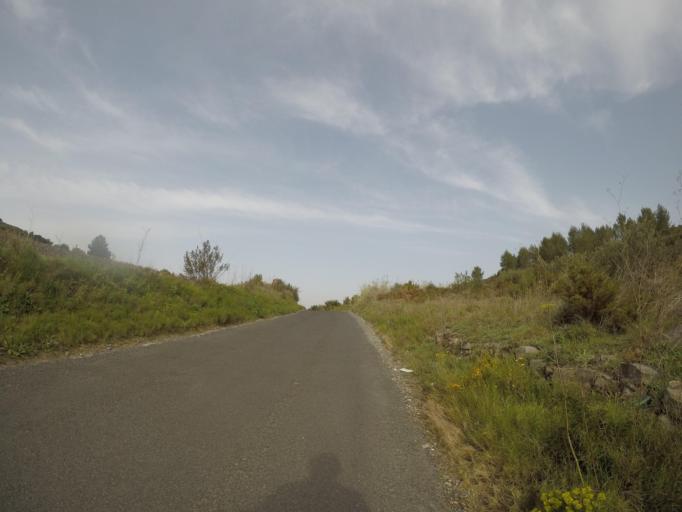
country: FR
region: Languedoc-Roussillon
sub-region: Departement des Pyrenees-Orientales
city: Baixas
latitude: 42.7707
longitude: 2.8048
